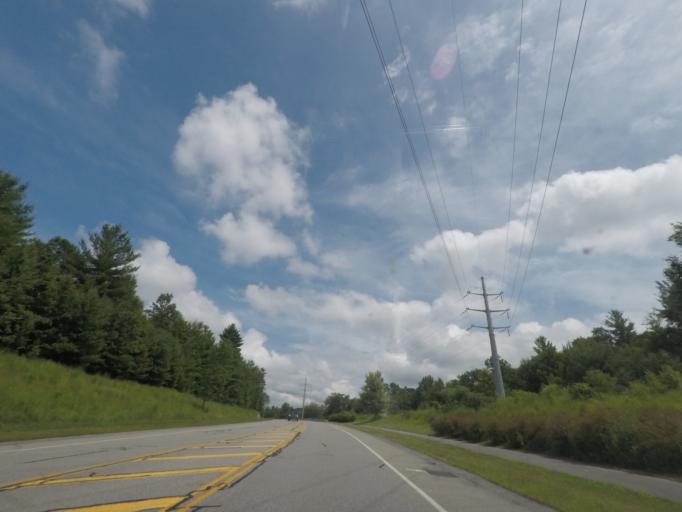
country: US
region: New York
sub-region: Saratoga County
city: Country Knolls
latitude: 42.9585
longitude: -73.7751
